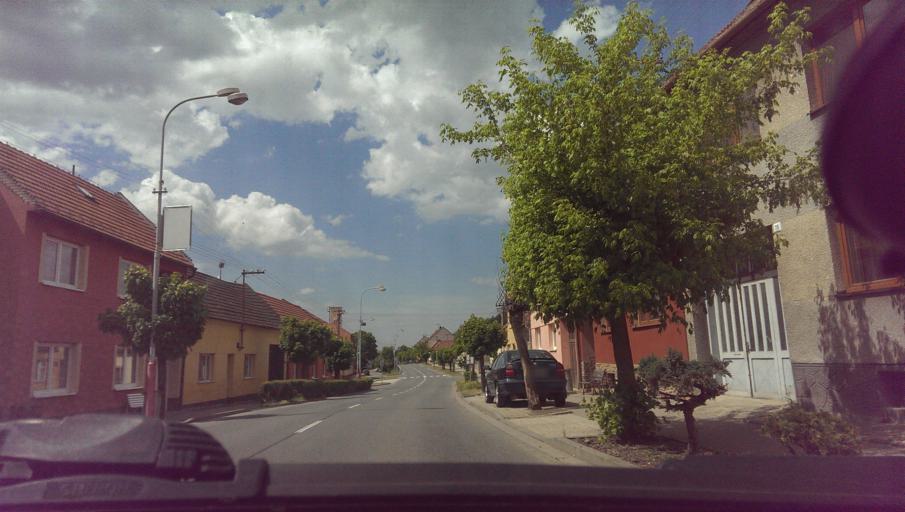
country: CZ
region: Zlin
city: Dolni Nemci
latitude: 48.9682
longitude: 17.5828
